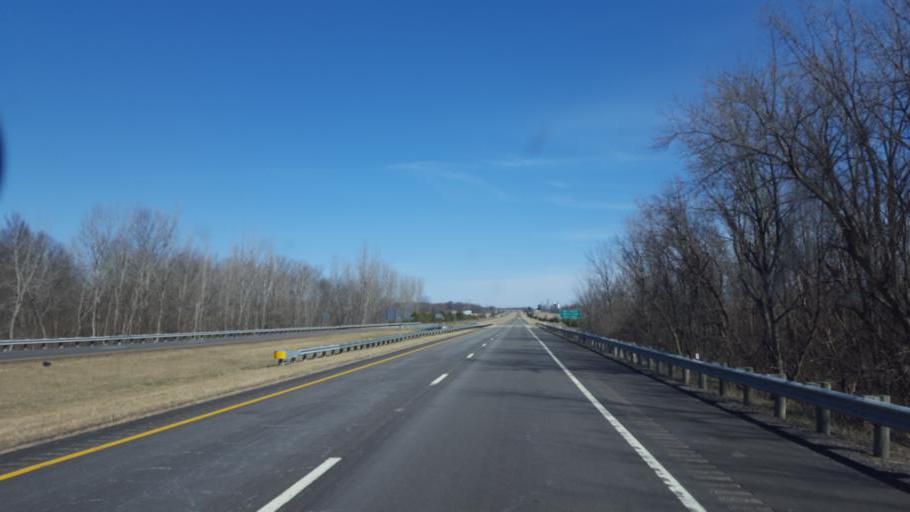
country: US
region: Ohio
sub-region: Knox County
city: Fredericktown
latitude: 40.4935
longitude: -82.5573
